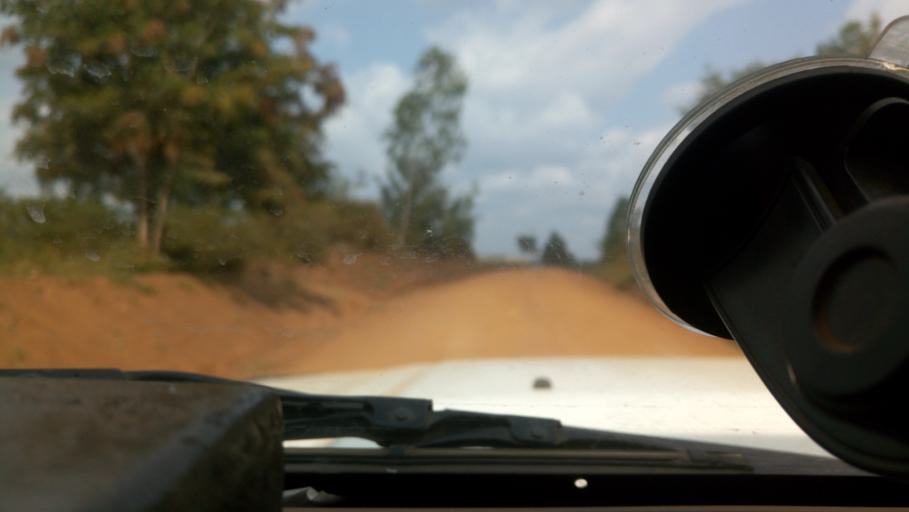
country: KE
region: Migori
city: Migori
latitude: -1.0884
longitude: 34.4215
